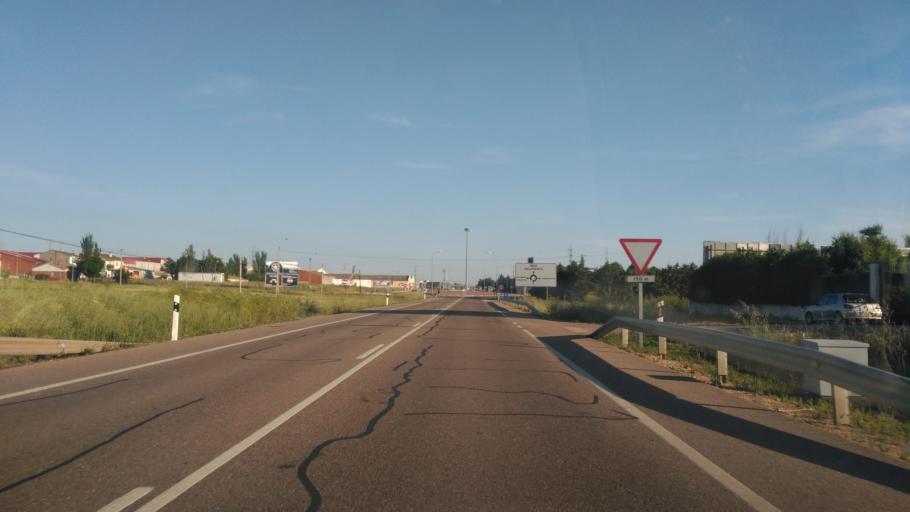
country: ES
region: Castille and Leon
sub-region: Provincia de Salamanca
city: Villares de la Reina
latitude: 41.0042
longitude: -5.6677
